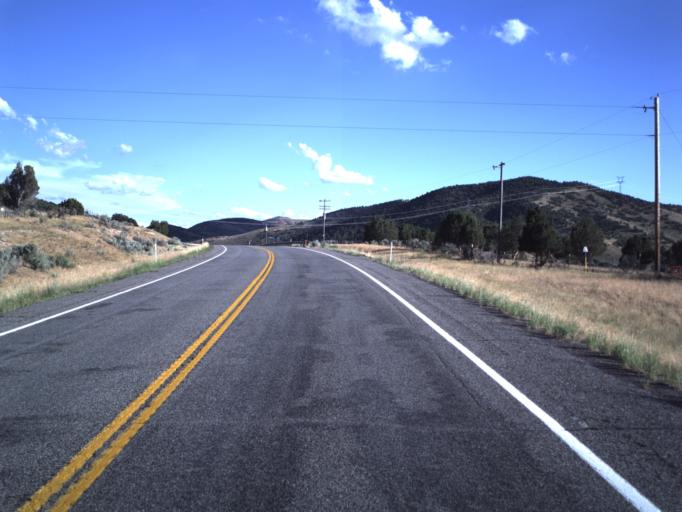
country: US
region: Utah
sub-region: Utah County
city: Woodland Hills
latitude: 39.8947
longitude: -111.5501
